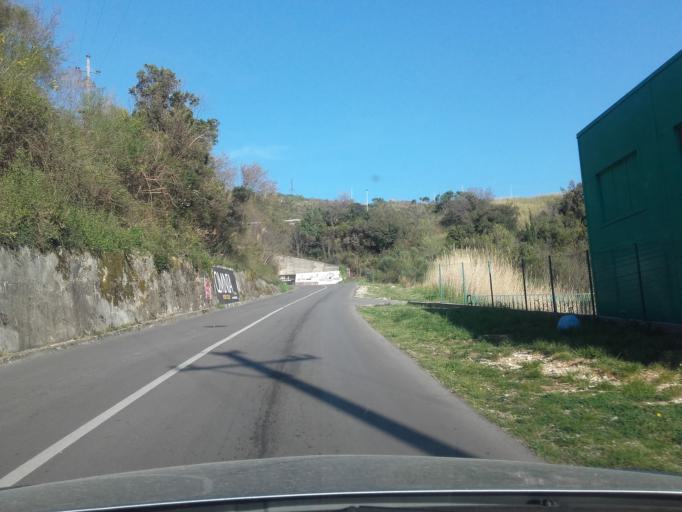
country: ME
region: Budva
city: Budva
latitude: 42.2905
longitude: 18.8257
